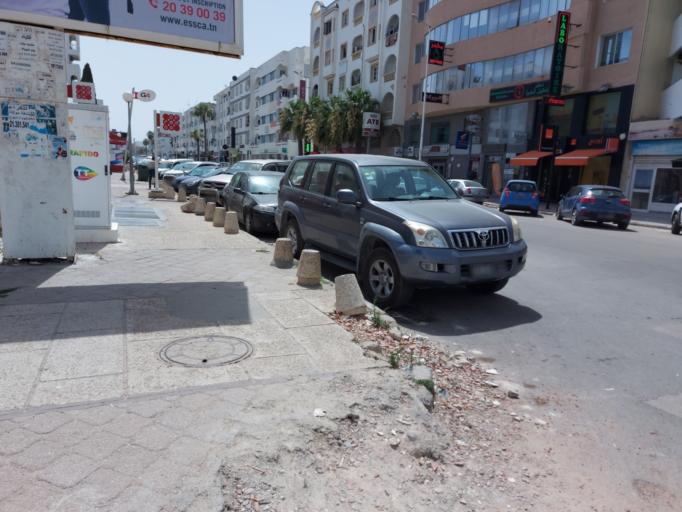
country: TN
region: Al Munastir
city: Monastir
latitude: 35.7714
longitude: 10.8244
